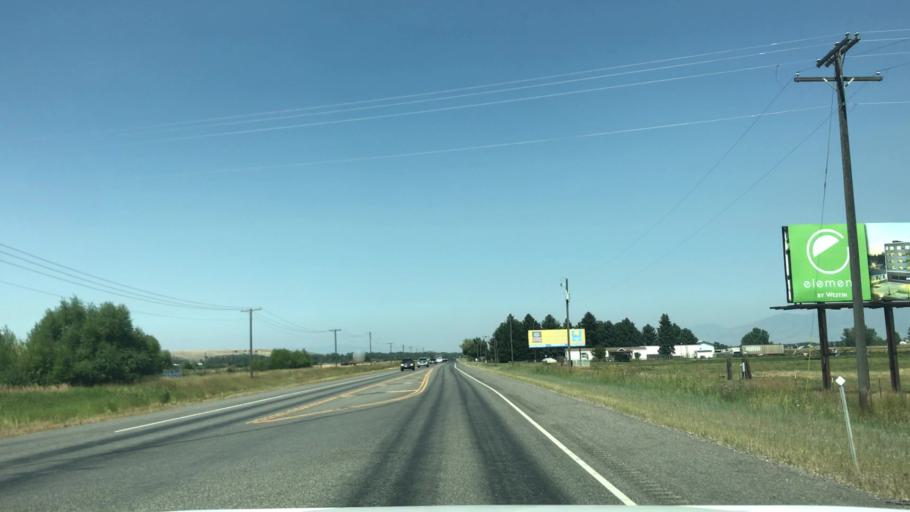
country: US
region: Montana
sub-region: Gallatin County
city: Four Corners
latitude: 45.6237
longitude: -111.1969
